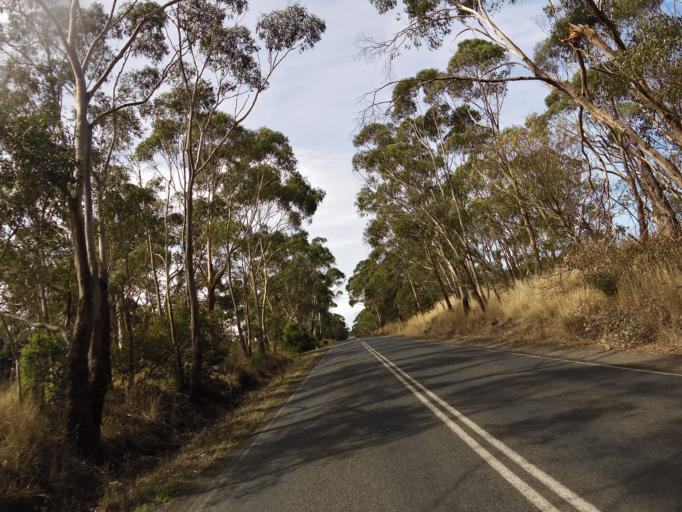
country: AU
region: Victoria
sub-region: Warrnambool
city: Allansford
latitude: -38.3922
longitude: 142.8983
